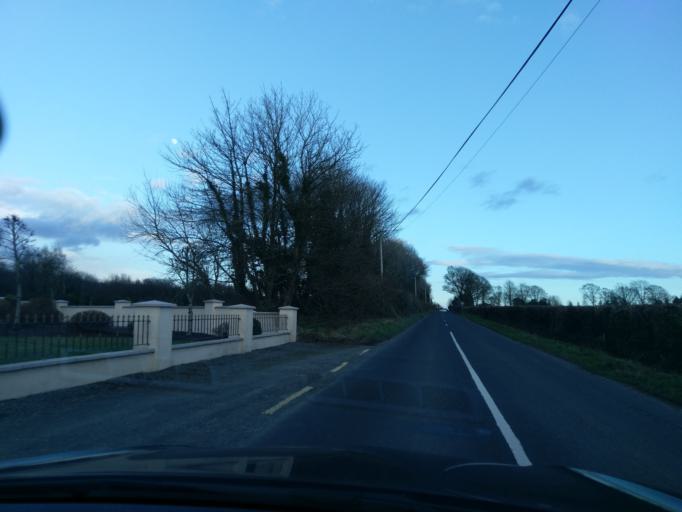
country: IE
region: Connaught
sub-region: County Galway
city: Athenry
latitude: 53.4304
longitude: -8.7012
